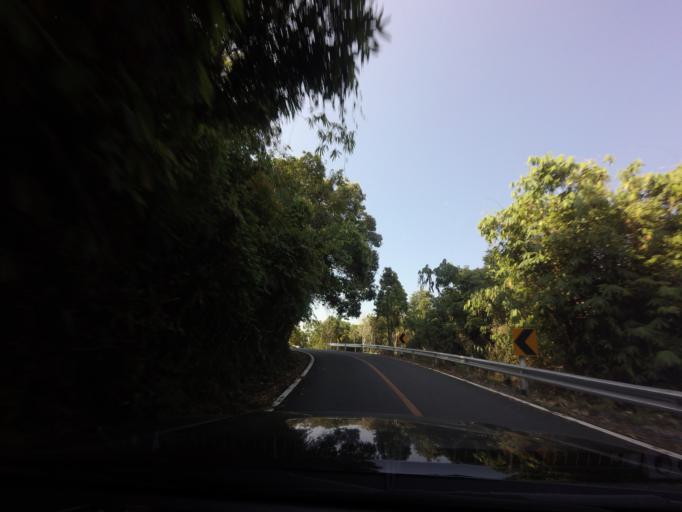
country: TH
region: Kanchanaburi
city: Thong Pha Phum
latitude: 14.6852
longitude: 98.4156
